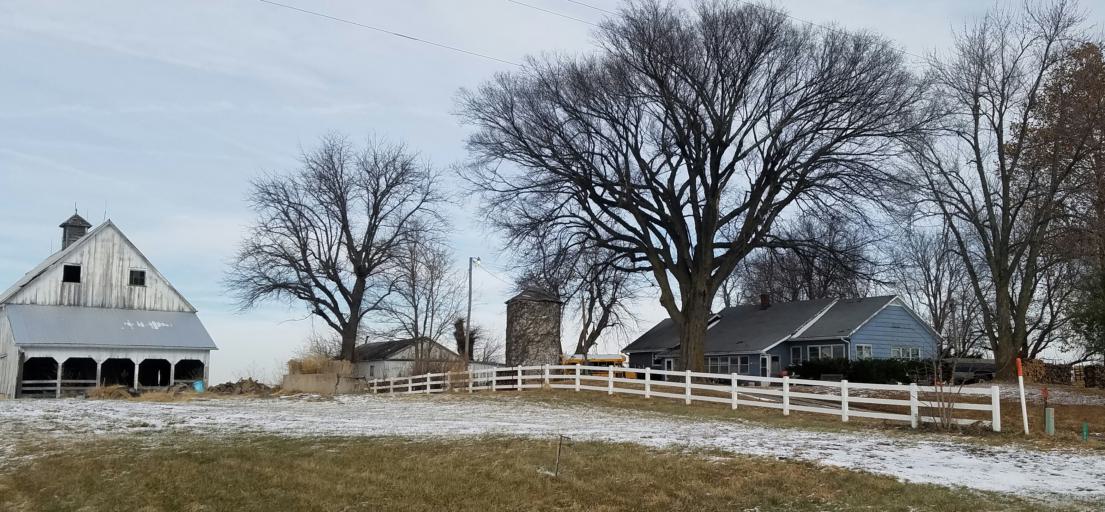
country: US
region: Missouri
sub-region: Lafayette County
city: Lexington
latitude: 39.1802
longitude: -93.7737
